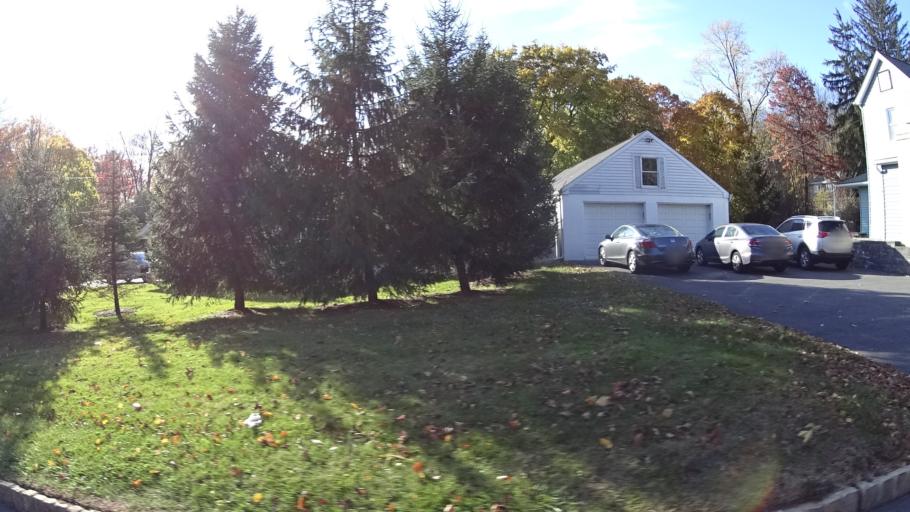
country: US
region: New Jersey
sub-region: Somerset County
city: Watchung
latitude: 40.6414
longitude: -74.4514
